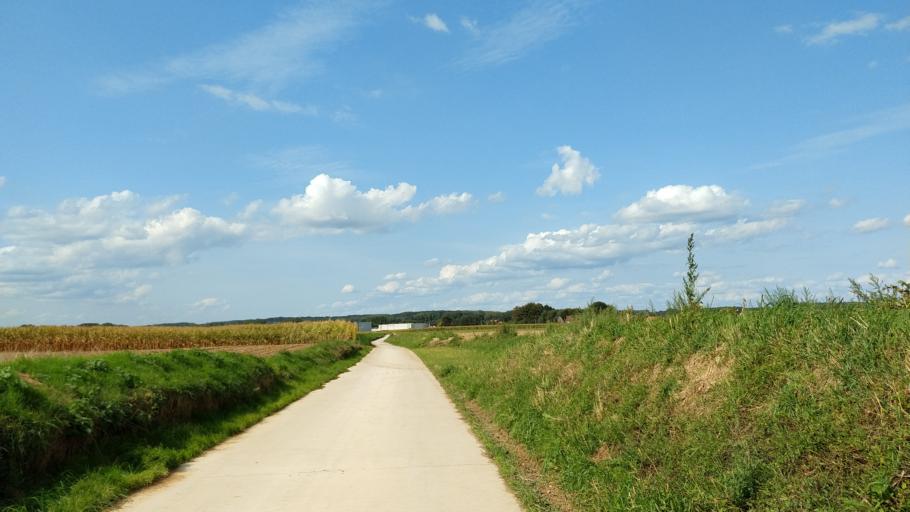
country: BE
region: Flanders
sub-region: Provincie Vlaams-Brabant
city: Boutersem
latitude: 50.8270
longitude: 4.8572
